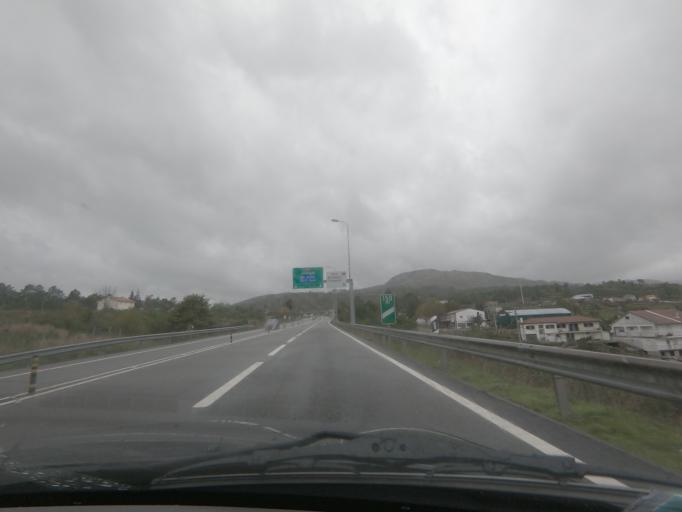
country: PT
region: Vila Real
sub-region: Vila Real
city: Vila Real
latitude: 41.2821
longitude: -7.8016
